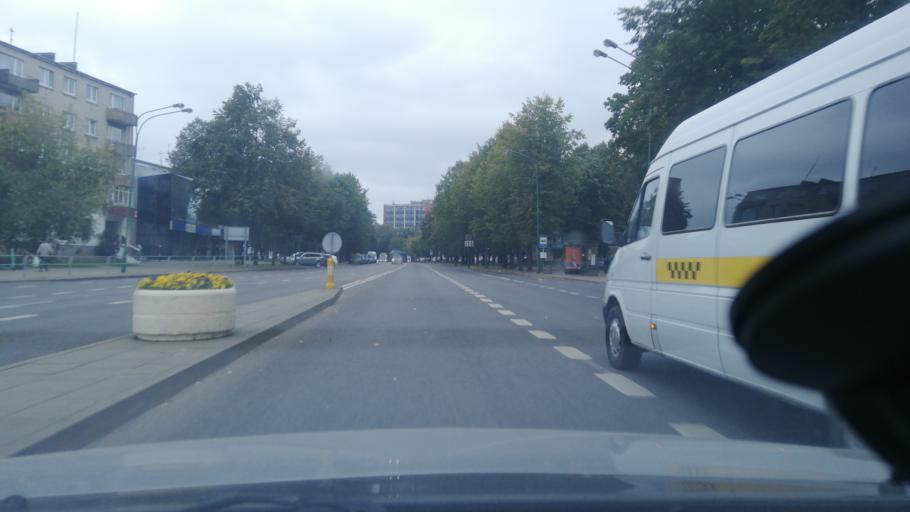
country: LT
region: Klaipedos apskritis
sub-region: Klaipeda
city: Klaipeda
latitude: 55.7035
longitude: 21.1436
